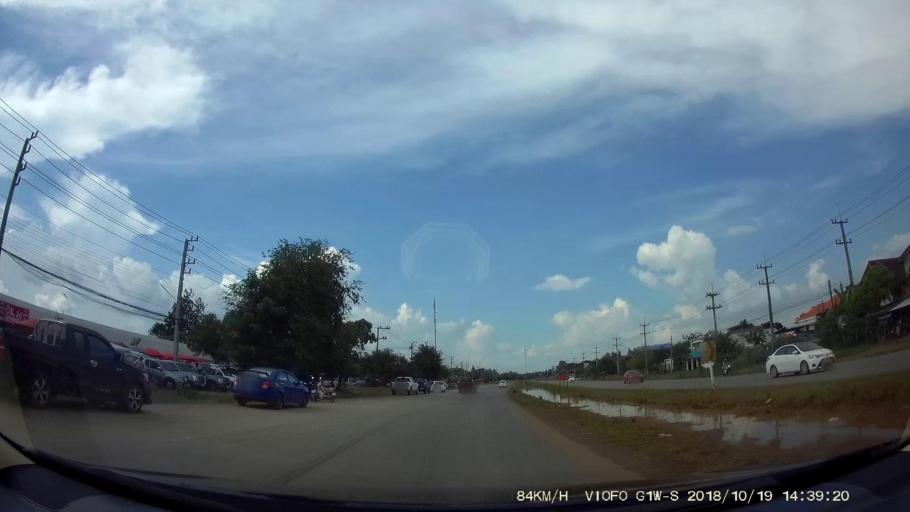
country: TH
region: Chaiyaphum
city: Kaeng Khro
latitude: 16.2247
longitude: 102.1953
